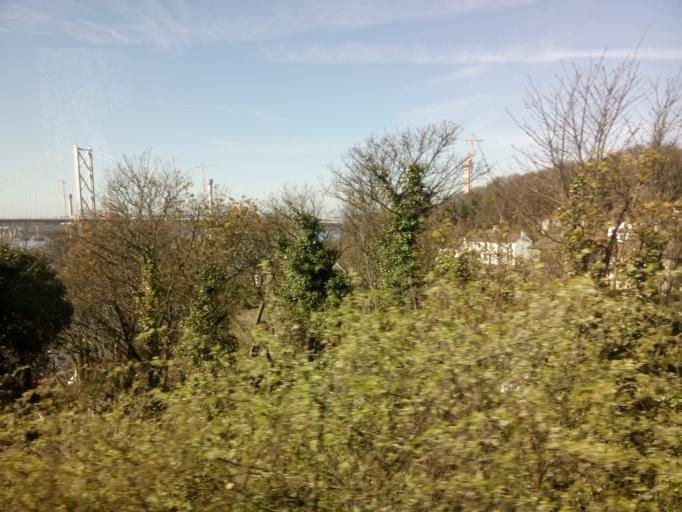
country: GB
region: Scotland
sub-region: Fife
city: North Queensferry
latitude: 56.0109
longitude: -3.3936
